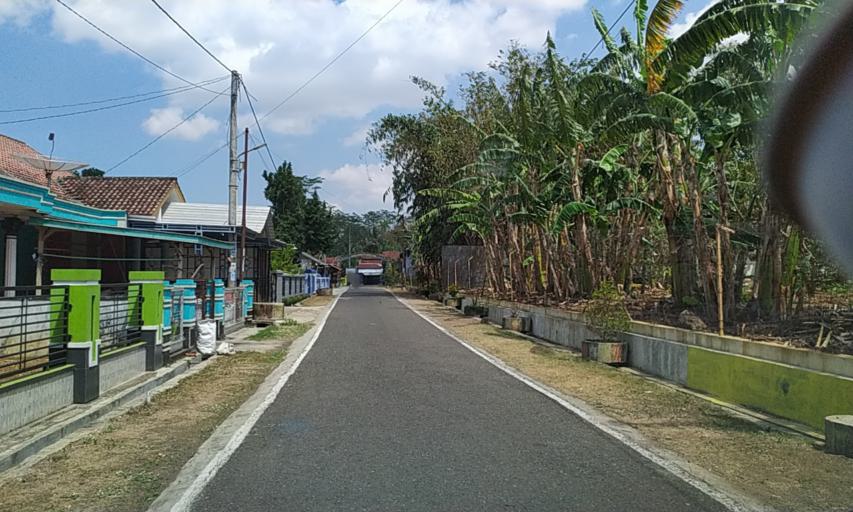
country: ID
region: Central Java
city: Kroya
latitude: -7.6329
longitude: 109.2382
